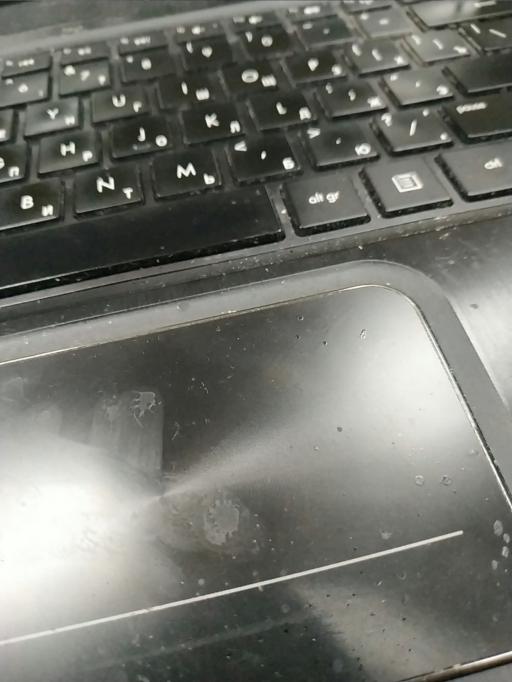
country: RU
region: Moscow
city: Vagonoremont
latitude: 55.8921
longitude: 37.5515
